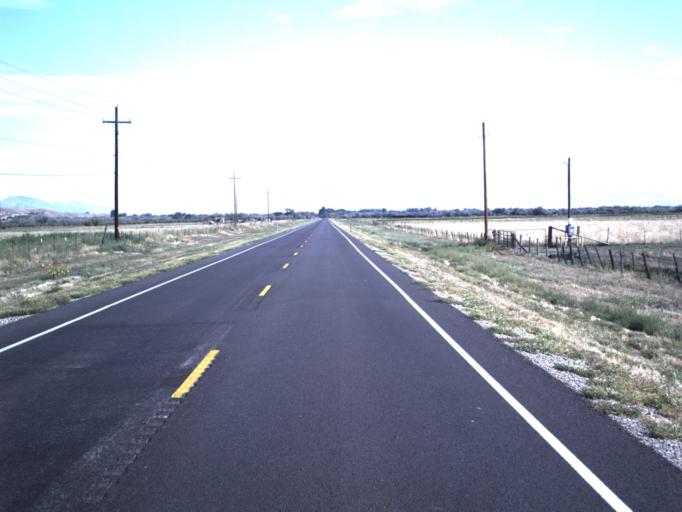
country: US
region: Utah
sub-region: Sevier County
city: Salina
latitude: 38.9791
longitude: -111.8605
